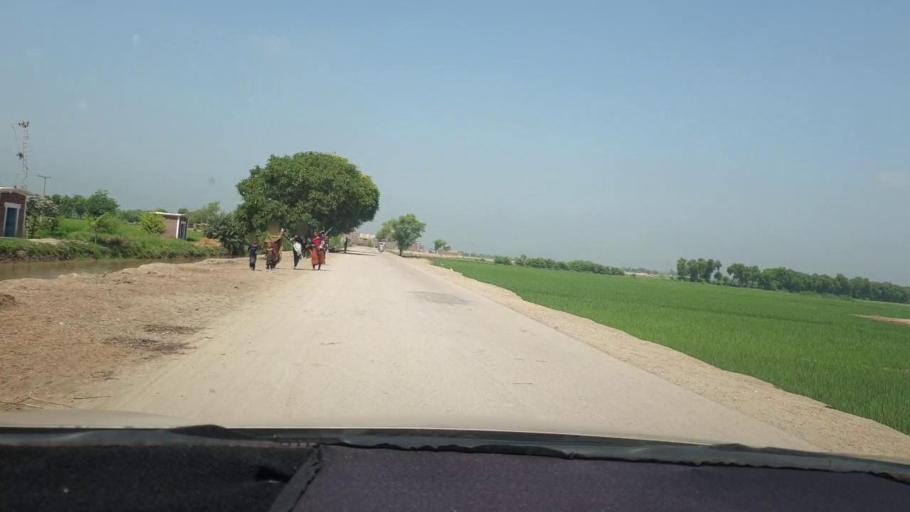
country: PK
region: Sindh
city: Miro Khan
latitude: 27.7719
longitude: 68.0609
